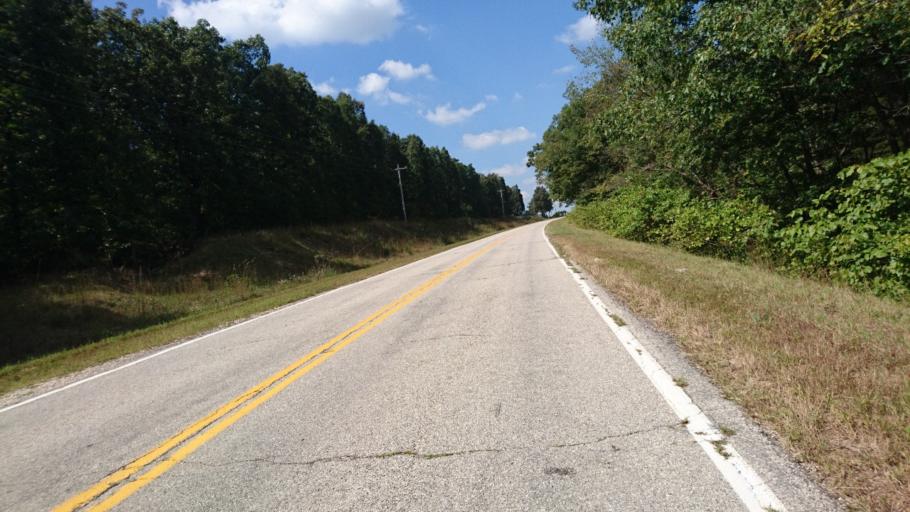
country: US
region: Missouri
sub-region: Pulaski County
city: Richland
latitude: 37.7525
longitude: -92.5011
